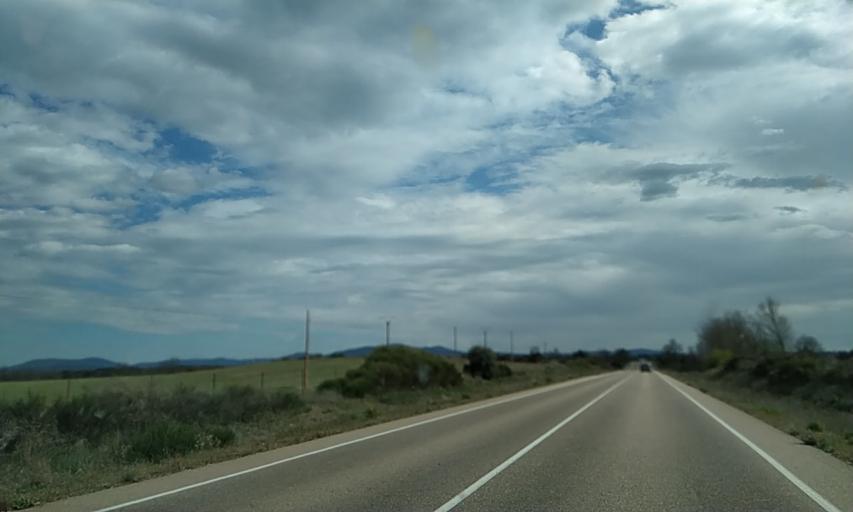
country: ES
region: Castille and Leon
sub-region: Provincia de Salamanca
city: Robleda
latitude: 40.4108
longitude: -6.6031
